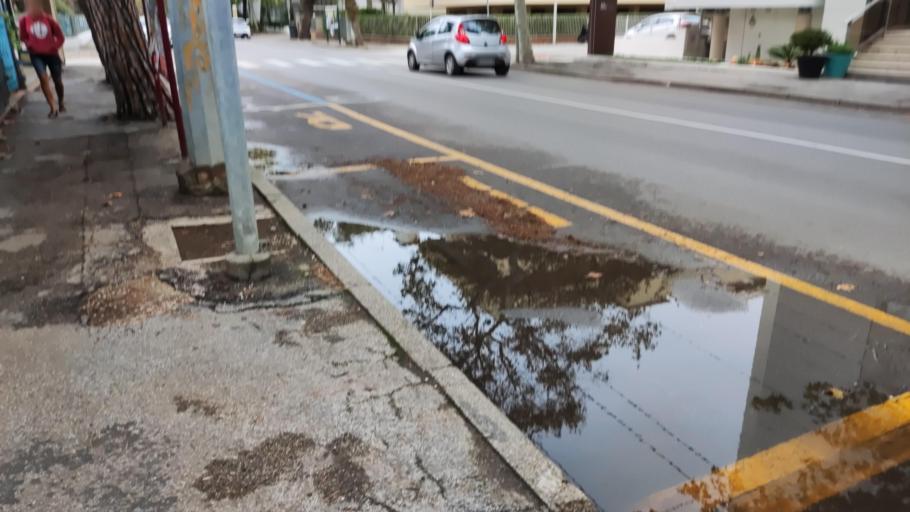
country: IT
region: Emilia-Romagna
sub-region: Provincia di Rimini
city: Riccione
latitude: 44.0082
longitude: 12.6528
